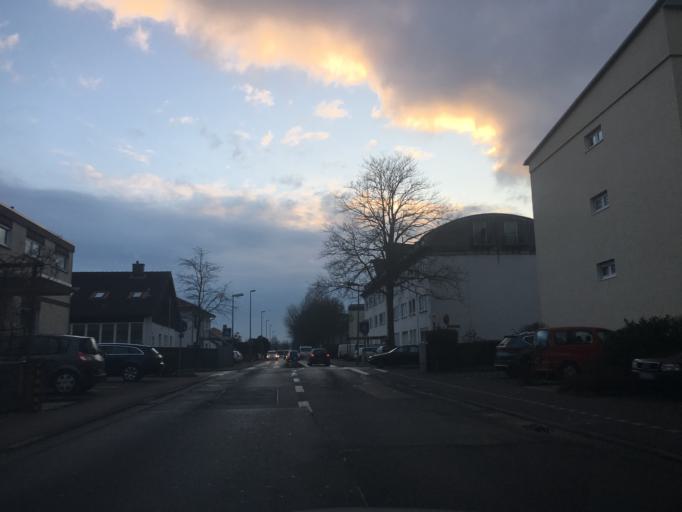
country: DE
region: Hesse
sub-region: Regierungsbezirk Darmstadt
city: Hattersheim
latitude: 50.0716
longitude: 8.5010
